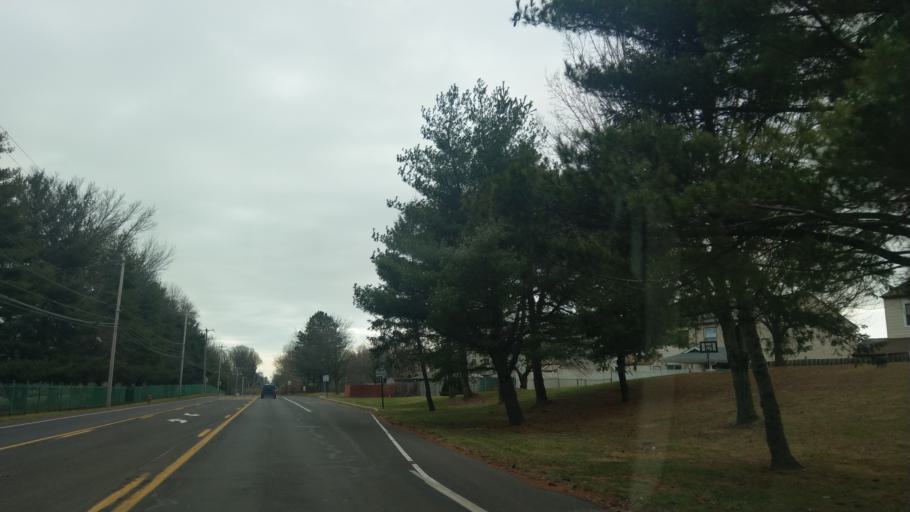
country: US
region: Pennsylvania
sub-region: Bucks County
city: Hulmeville
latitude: 40.1239
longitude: -74.9267
